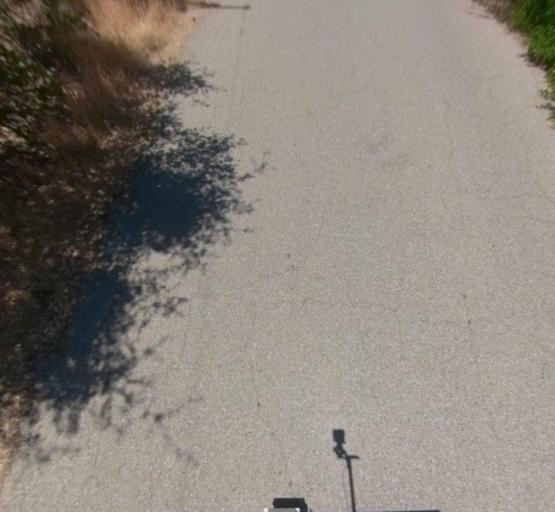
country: US
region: California
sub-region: Fresno County
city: Auberry
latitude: 37.2051
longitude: -119.5595
